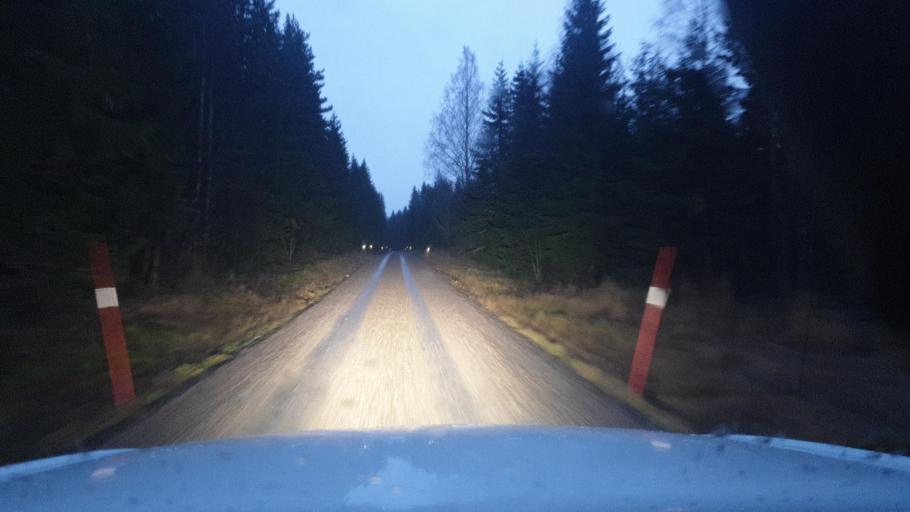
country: SE
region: Vaermland
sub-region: Eda Kommun
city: Charlottenberg
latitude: 60.0353
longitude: 12.6308
